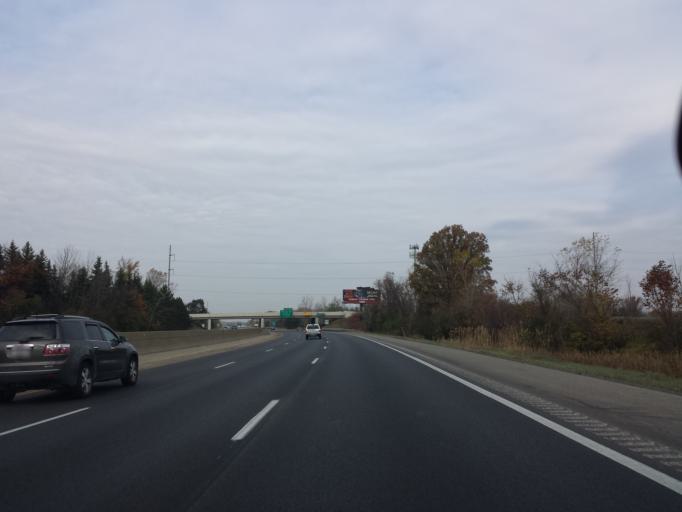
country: US
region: Michigan
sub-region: Genesee County
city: Flint
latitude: 43.0442
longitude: -83.7540
